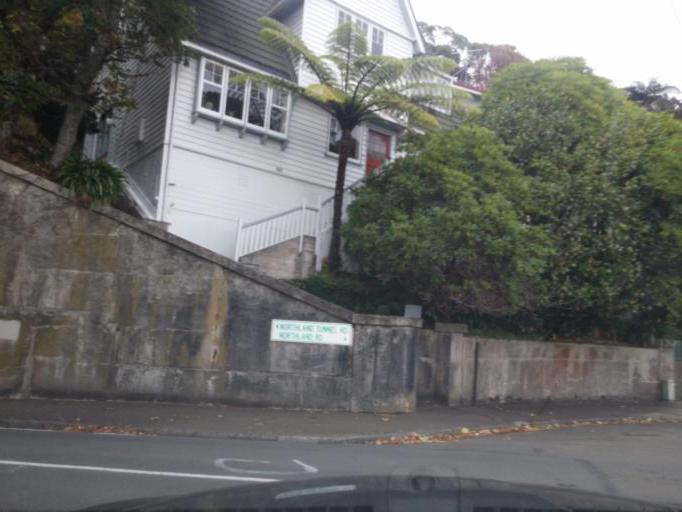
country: NZ
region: Wellington
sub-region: Wellington City
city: Kelburn
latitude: -41.2842
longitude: 174.7561
